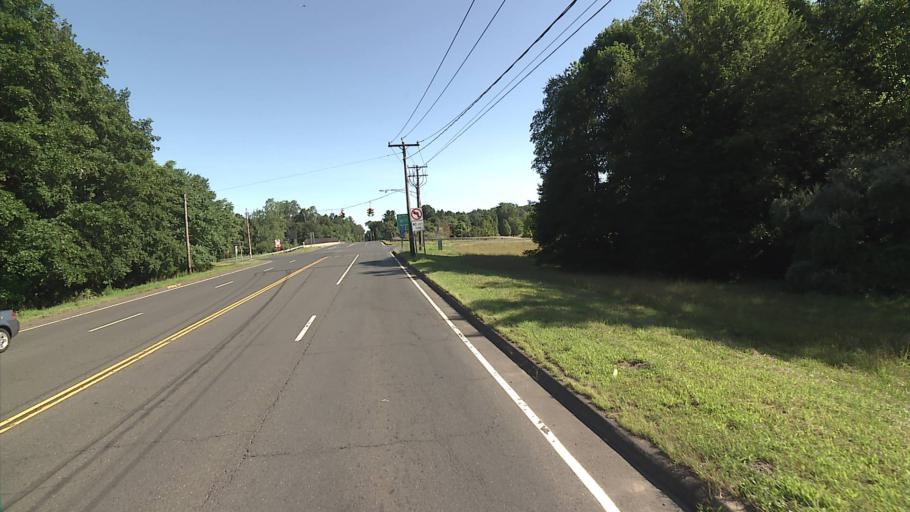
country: US
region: Connecticut
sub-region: New Haven County
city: Cheshire Village
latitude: 41.5555
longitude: -72.8907
